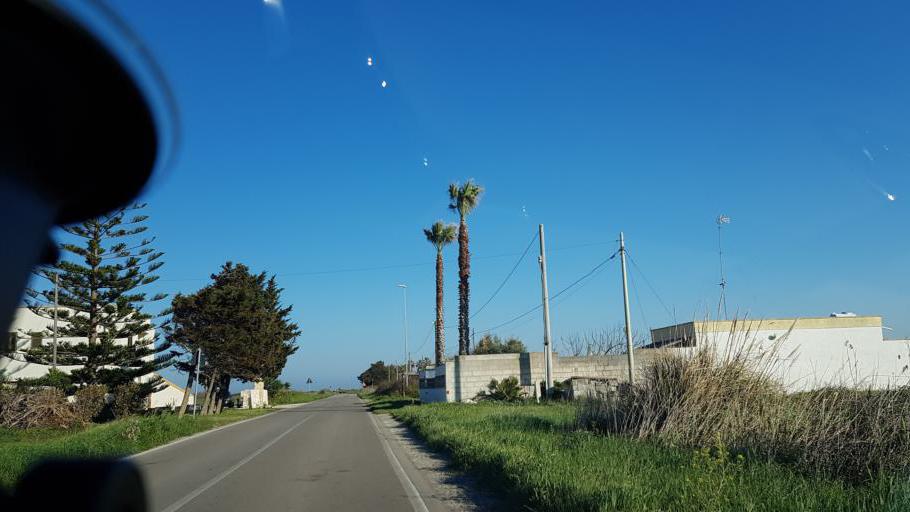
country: IT
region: Apulia
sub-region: Provincia di Lecce
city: Giorgilorio
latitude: 40.4499
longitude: 18.2238
